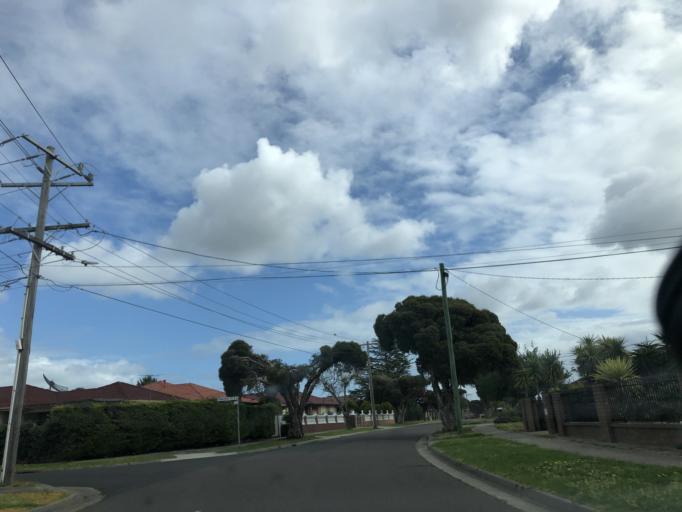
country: AU
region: Victoria
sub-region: Kingston
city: Clayton South
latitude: -37.9397
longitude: 145.1116
